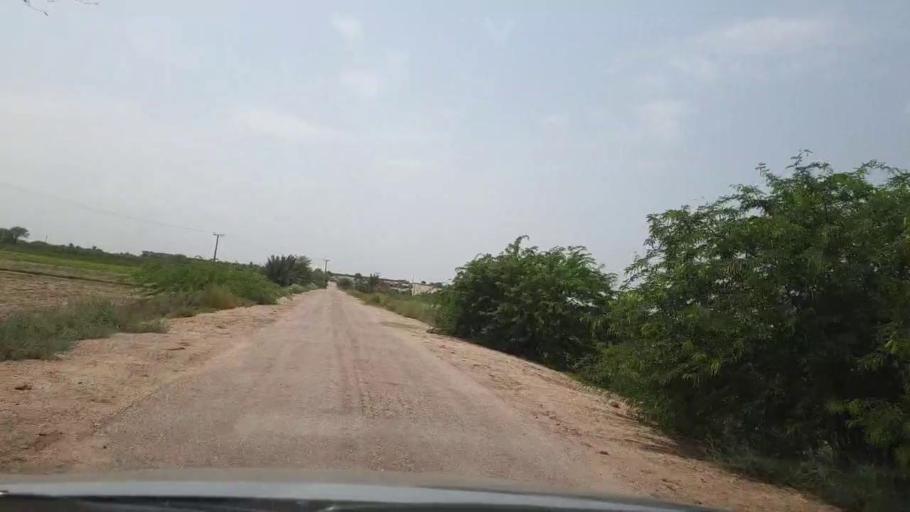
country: PK
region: Sindh
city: Pano Aqil
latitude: 27.5905
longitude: 69.1994
